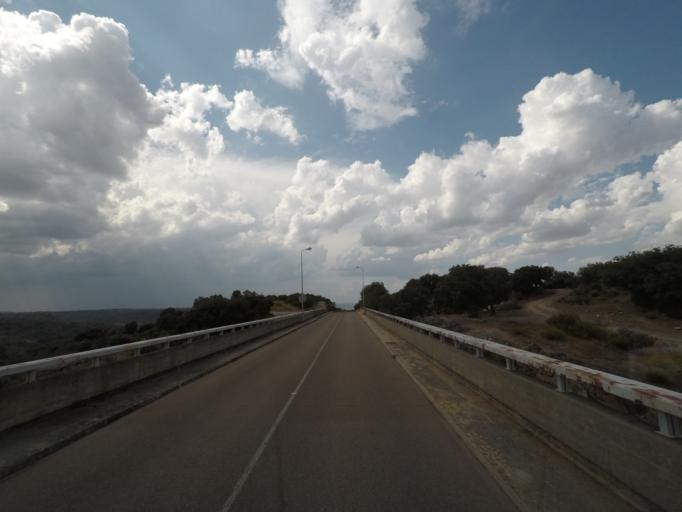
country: ES
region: Castille and Leon
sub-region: Provincia de Salamanca
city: Almendra
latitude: 41.2753
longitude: -6.3265
